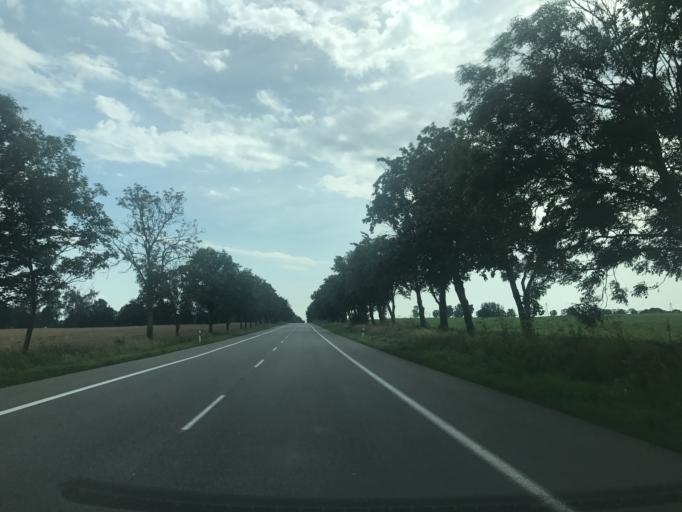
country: PL
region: Warmian-Masurian Voivodeship
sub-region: Powiat ostrodzki
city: Gierzwald
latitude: 53.6359
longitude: 20.0576
